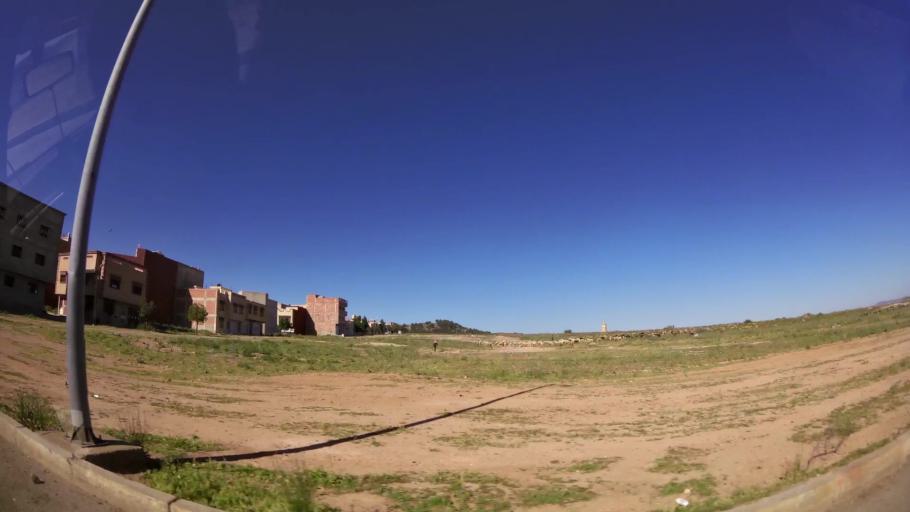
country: MA
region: Oriental
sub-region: Oujda-Angad
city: Oujda
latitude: 34.6494
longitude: -1.8867
